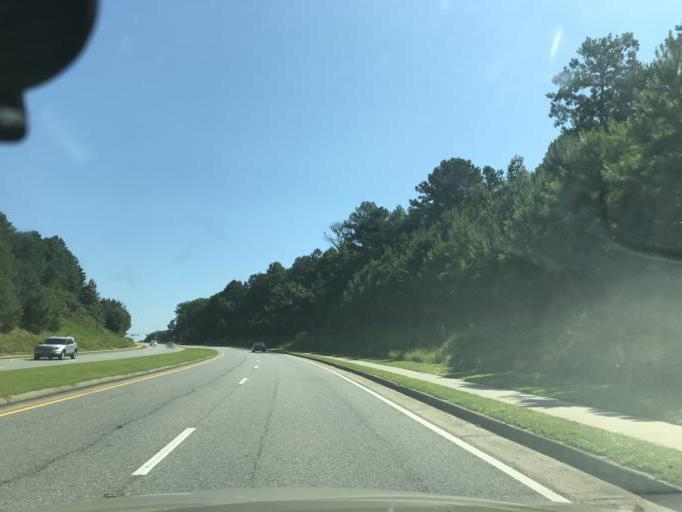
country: US
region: Georgia
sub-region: Forsyth County
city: Cumming
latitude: 34.2031
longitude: -84.1204
